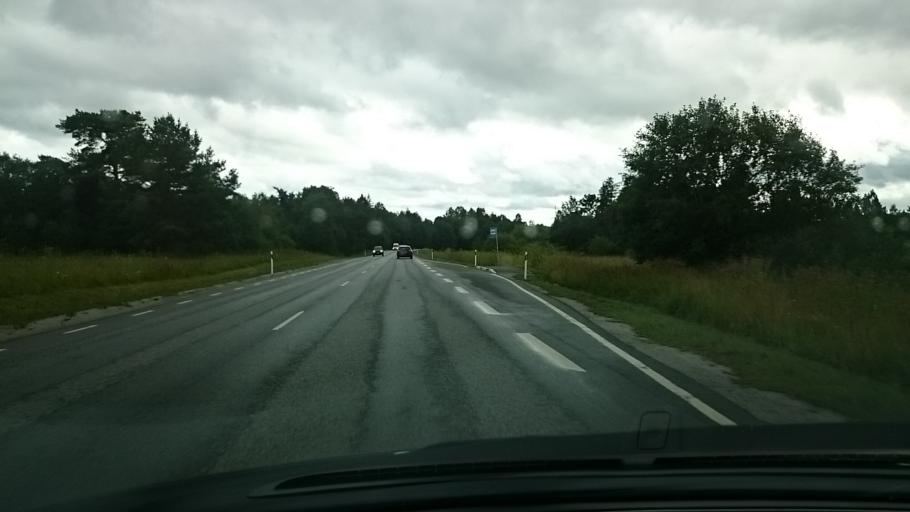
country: EE
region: Harju
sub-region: Keila linn
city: Keila
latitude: 59.2651
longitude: 24.2916
